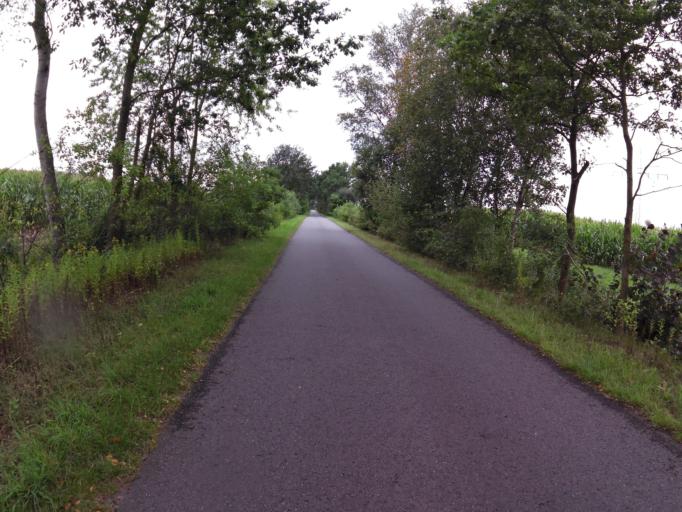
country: DE
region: Lower Saxony
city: Rotenburg
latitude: 53.1415
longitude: 9.4392
